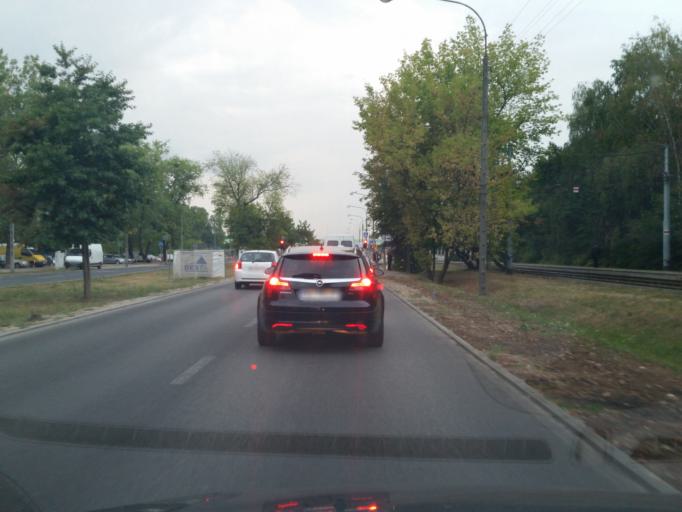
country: PL
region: Masovian Voivodeship
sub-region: Warszawa
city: Bielany
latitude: 52.2970
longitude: 20.9435
